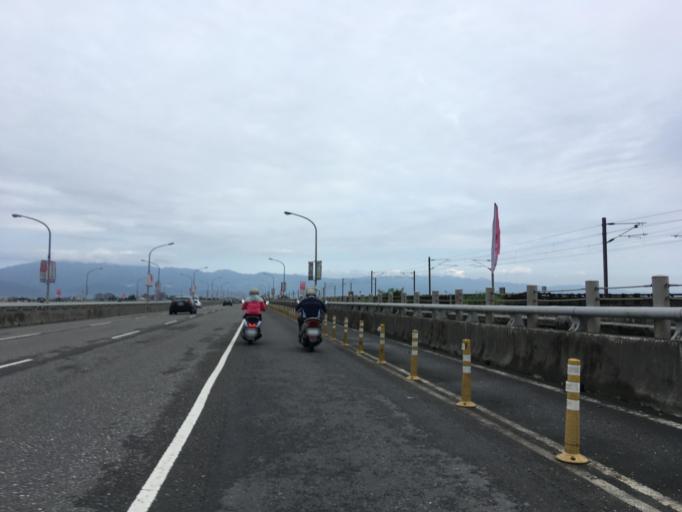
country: TW
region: Taiwan
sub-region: Yilan
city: Yilan
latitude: 24.7120
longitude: 121.7723
